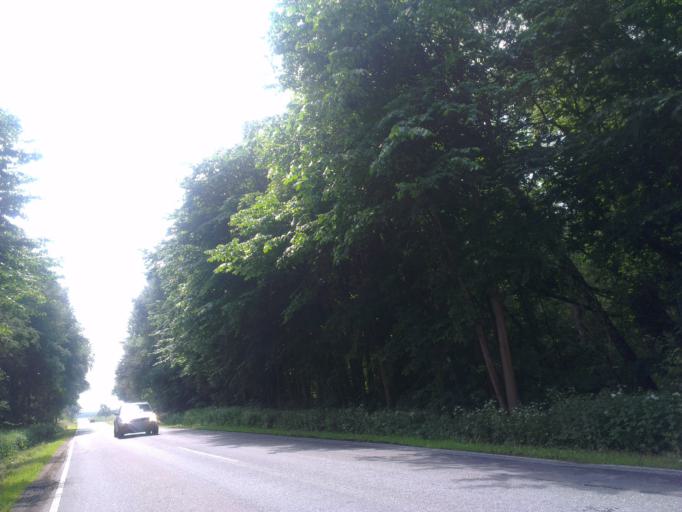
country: DK
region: Capital Region
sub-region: Frederikssund Kommune
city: Jaegerspris
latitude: 55.8726
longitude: 11.9592
